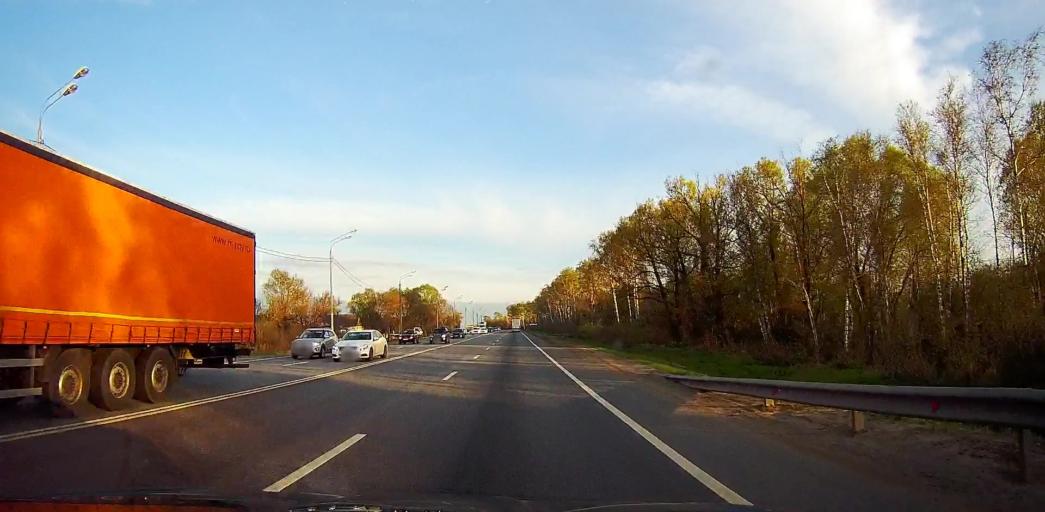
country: RU
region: Moskovskaya
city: Troitskoye
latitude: 55.2728
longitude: 38.4977
